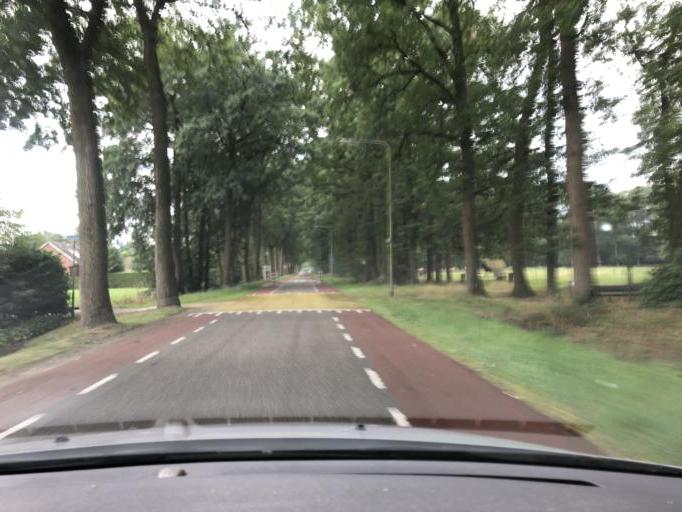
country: NL
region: Overijssel
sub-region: Gemeente Dalfsen
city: Dalfsen
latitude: 52.5712
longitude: 6.2937
